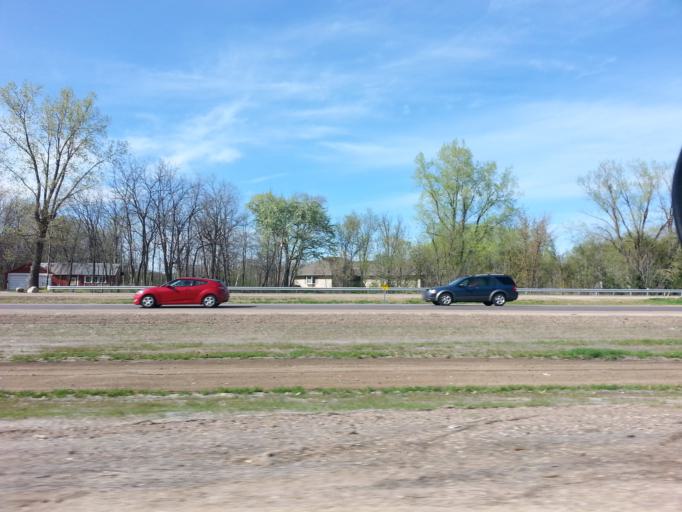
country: US
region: Minnesota
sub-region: Washington County
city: Mahtomedi
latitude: 45.0357
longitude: -92.9434
